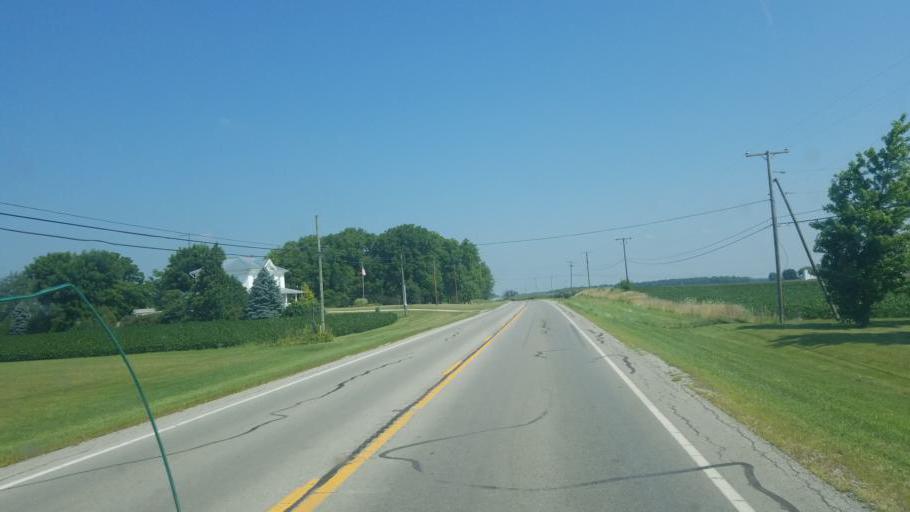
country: US
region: Ohio
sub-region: Hardin County
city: Kenton
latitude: 40.6727
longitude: -83.6118
